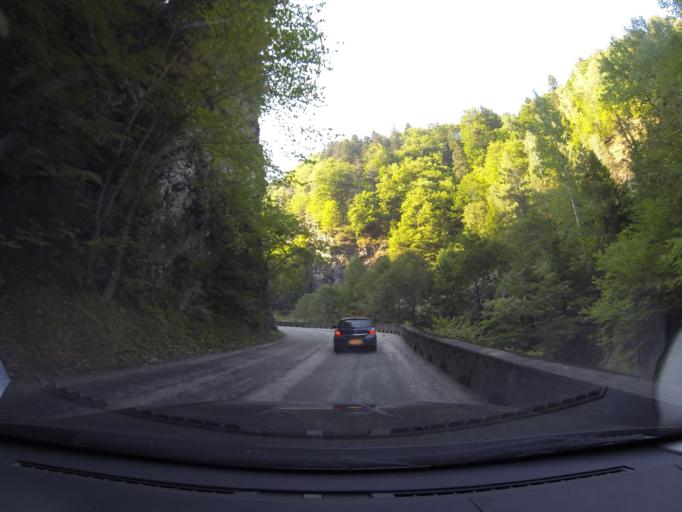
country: RO
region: Arges
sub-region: Comuna Arefu
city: Arefu
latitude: 45.3586
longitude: 24.6292
